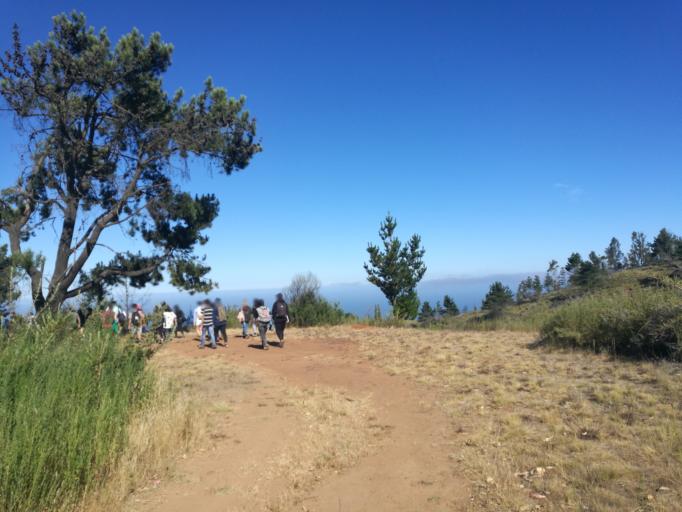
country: CL
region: Valparaiso
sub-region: Provincia de Valparaiso
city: Valparaiso
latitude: -33.0706
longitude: -71.6513
